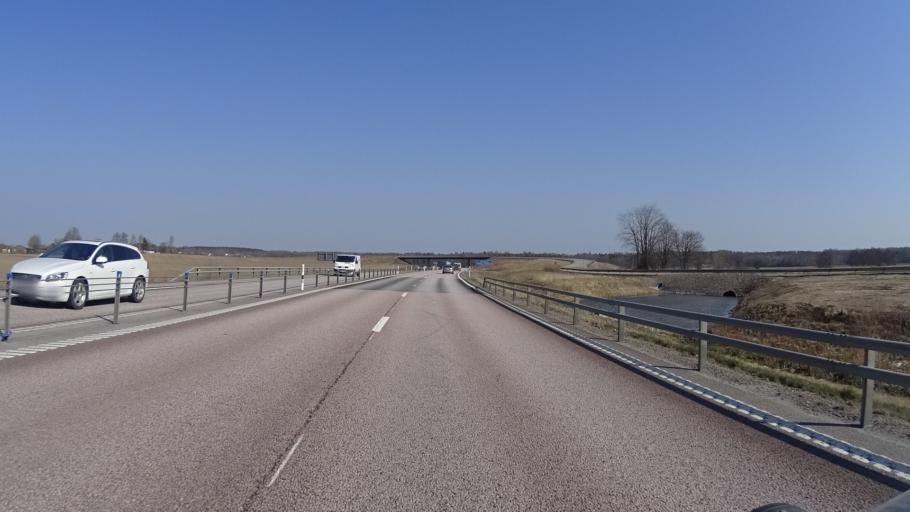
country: SE
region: OEstergoetland
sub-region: Motala Kommun
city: Motala
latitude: 58.4979
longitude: 15.0275
